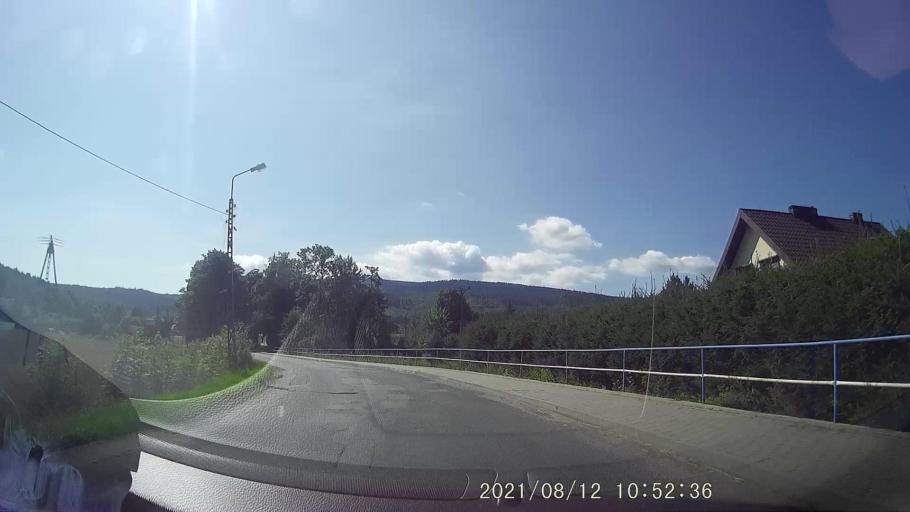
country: PL
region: Lower Silesian Voivodeship
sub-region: Powiat klodzki
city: Szczytna
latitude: 50.4110
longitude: 16.4486
